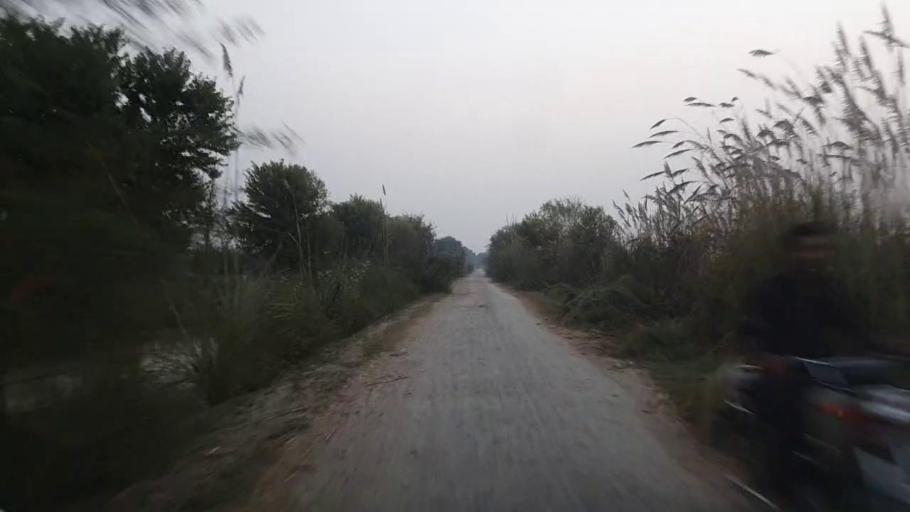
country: PK
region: Sindh
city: Karaundi
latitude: 26.9346
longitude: 68.4418
